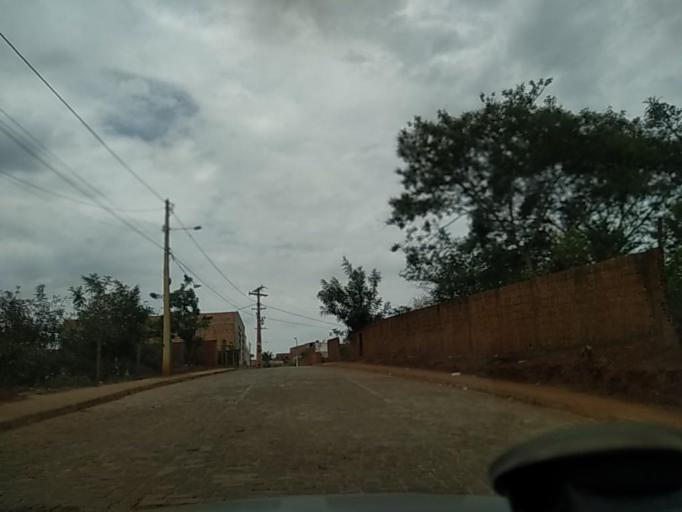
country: BR
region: Bahia
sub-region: Caetite
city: Caetite
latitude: -14.0533
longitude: -42.4777
